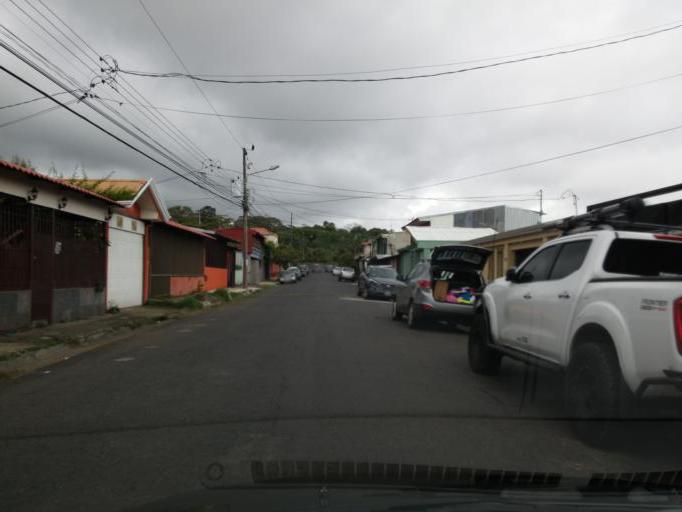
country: CR
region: Heredia
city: Mercedes
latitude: 10.0251
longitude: -84.1258
